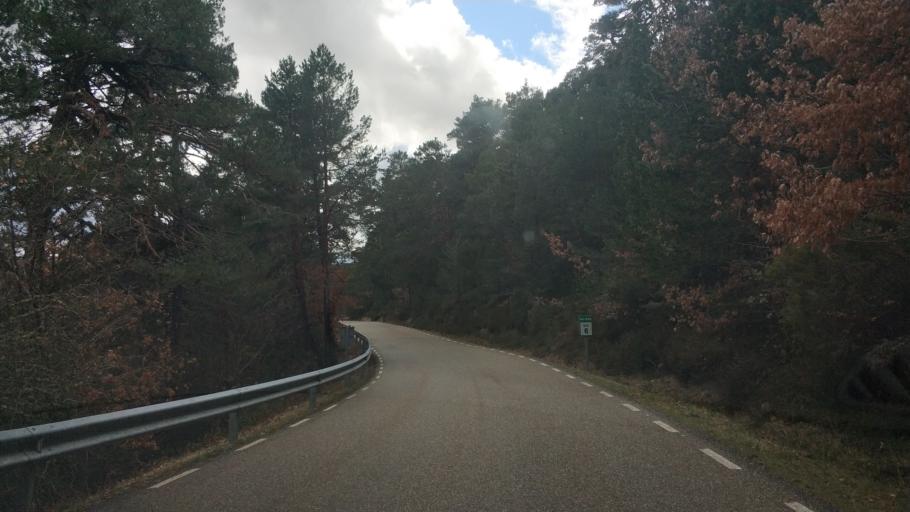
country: ES
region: Castille and Leon
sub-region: Provincia de Burgos
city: Quintanar de la Sierra
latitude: 42.0157
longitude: -3.0180
